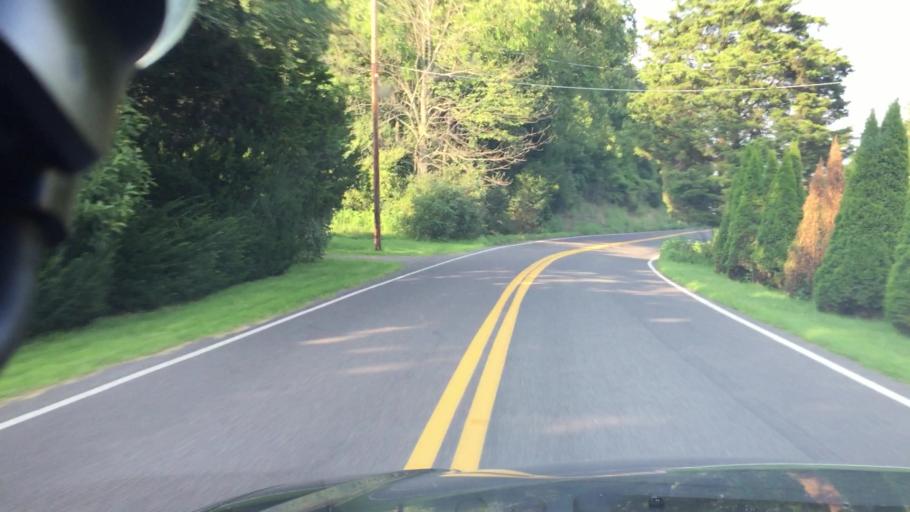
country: US
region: Pennsylvania
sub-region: Columbia County
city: Almedia
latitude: 40.9774
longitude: -76.3716
